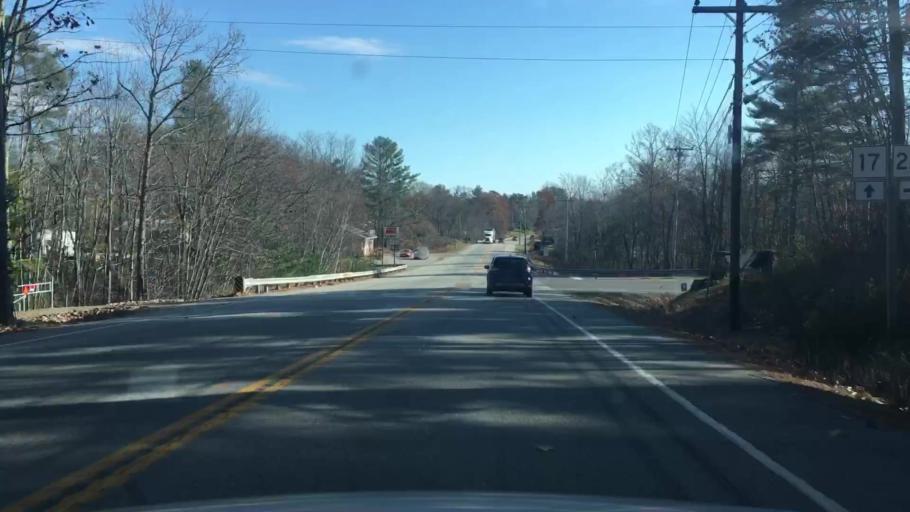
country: US
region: Maine
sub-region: Kennebec County
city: Chelsea
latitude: 44.2784
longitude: -69.6851
